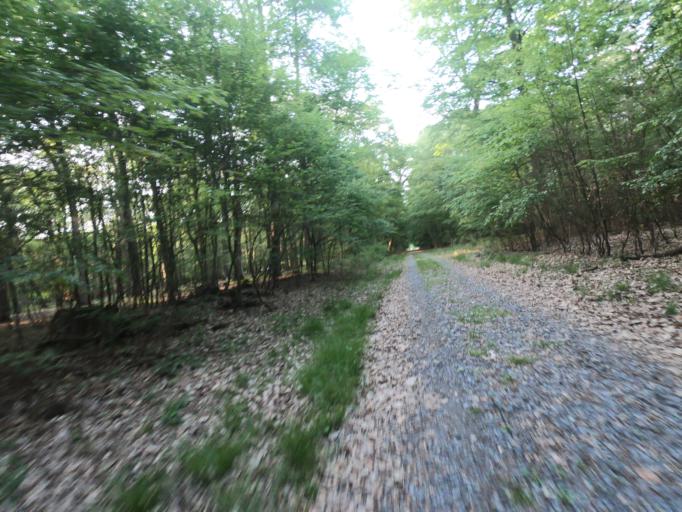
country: DE
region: Hesse
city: Morfelden-Walldorf
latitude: 49.9893
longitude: 8.5509
